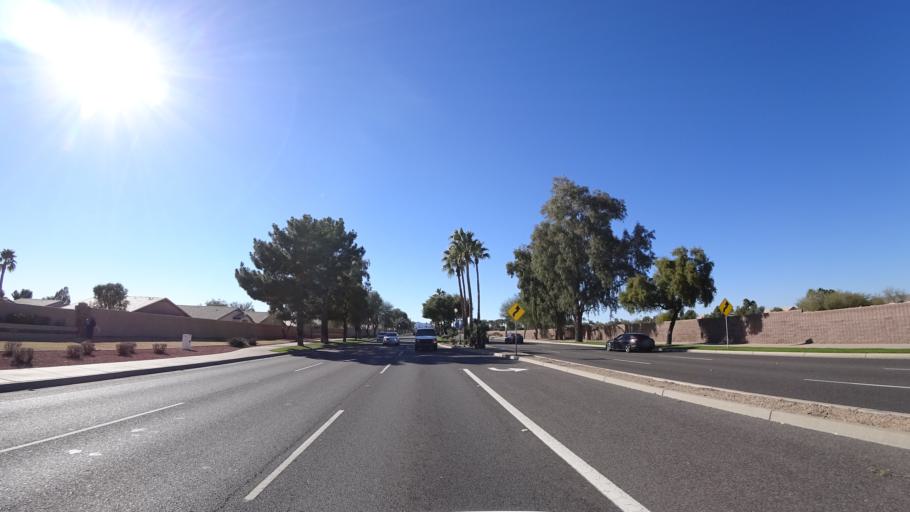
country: US
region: Arizona
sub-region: Maricopa County
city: Sun City West
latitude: 33.6387
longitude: -112.4002
